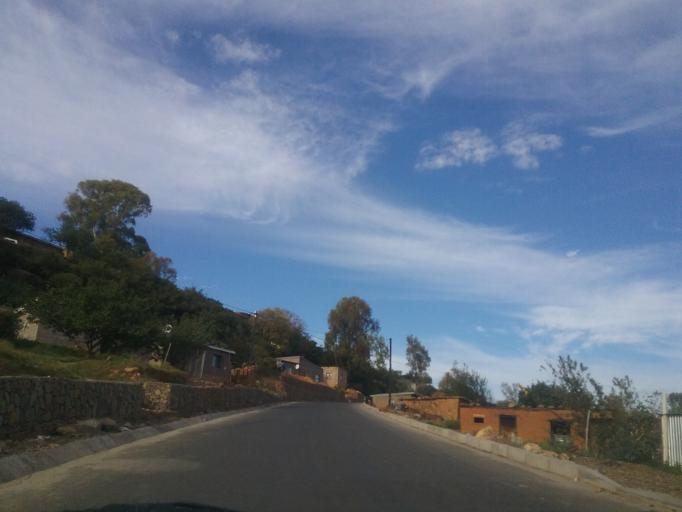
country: LS
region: Quthing
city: Quthing
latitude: -30.4031
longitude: 27.7044
